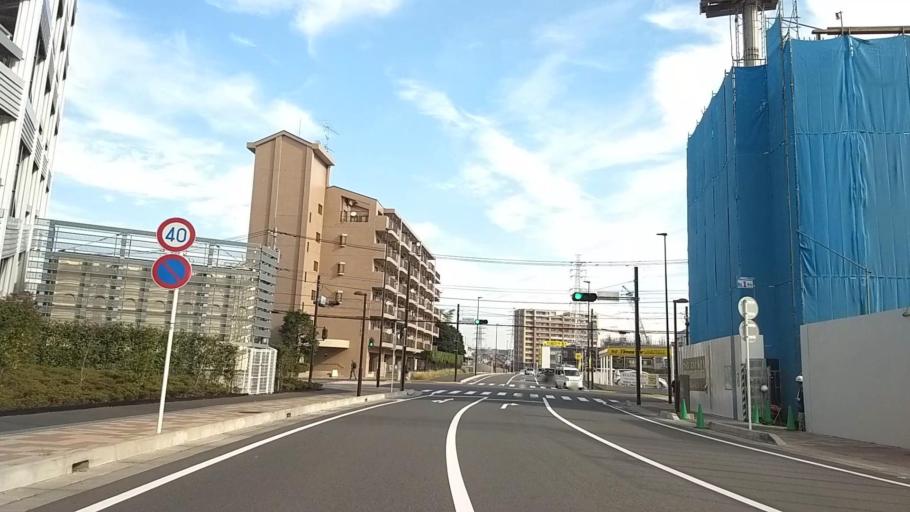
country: JP
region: Kanagawa
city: Zama
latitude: 35.4560
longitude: 139.3900
